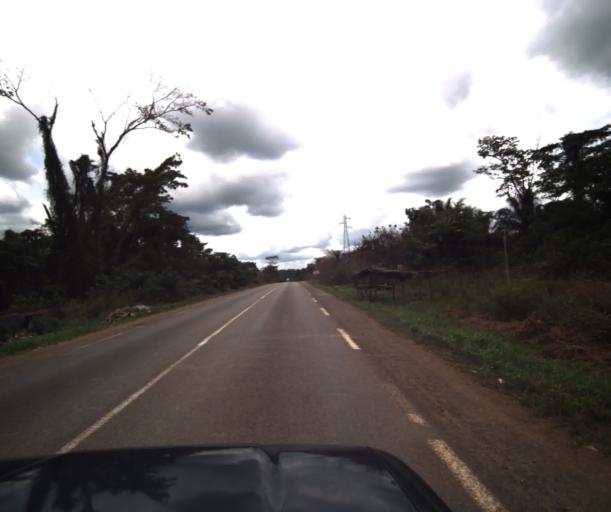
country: CM
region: Littoral
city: Edea
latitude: 3.8465
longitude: 10.4757
